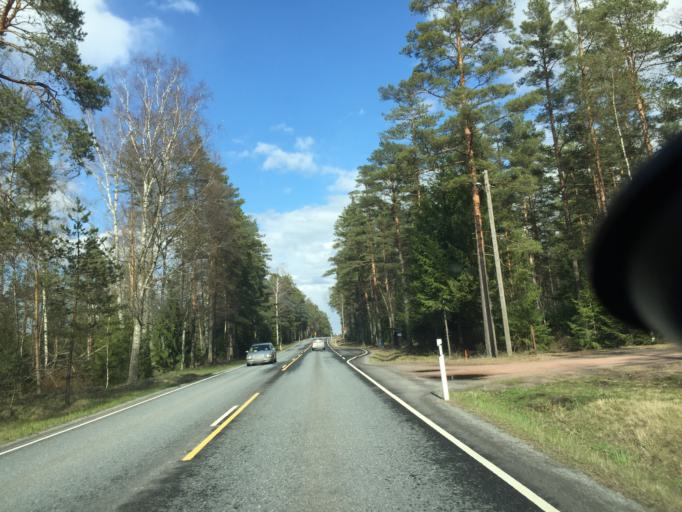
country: FI
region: Uusimaa
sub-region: Raaseporin
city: Karis
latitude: 60.1106
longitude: 23.7928
